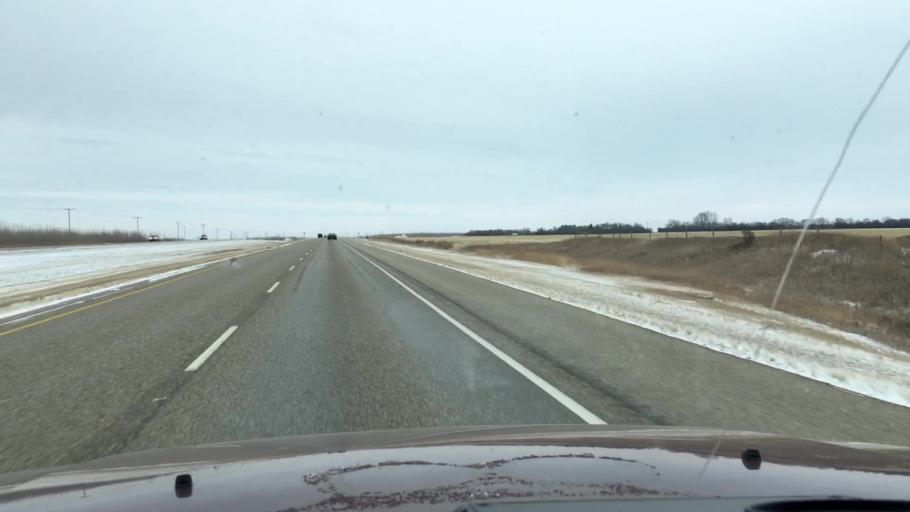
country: CA
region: Saskatchewan
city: Watrous
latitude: 51.0582
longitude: -105.8173
